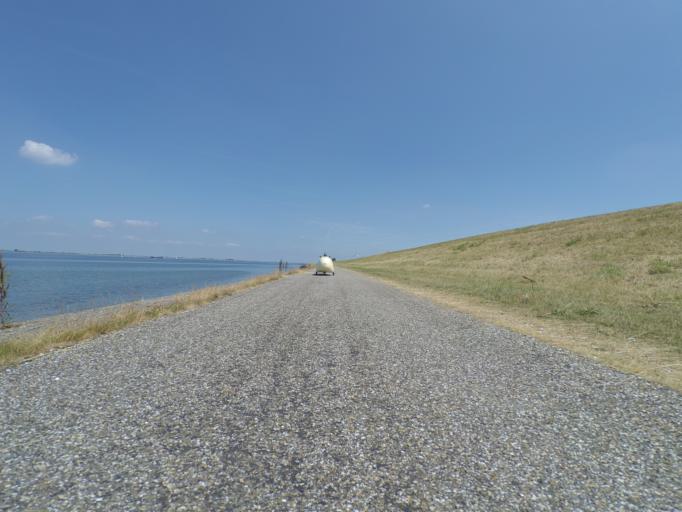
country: NL
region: Zeeland
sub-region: Schouwen-Duiveland
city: Bruinisse
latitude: 51.5975
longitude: 4.0257
